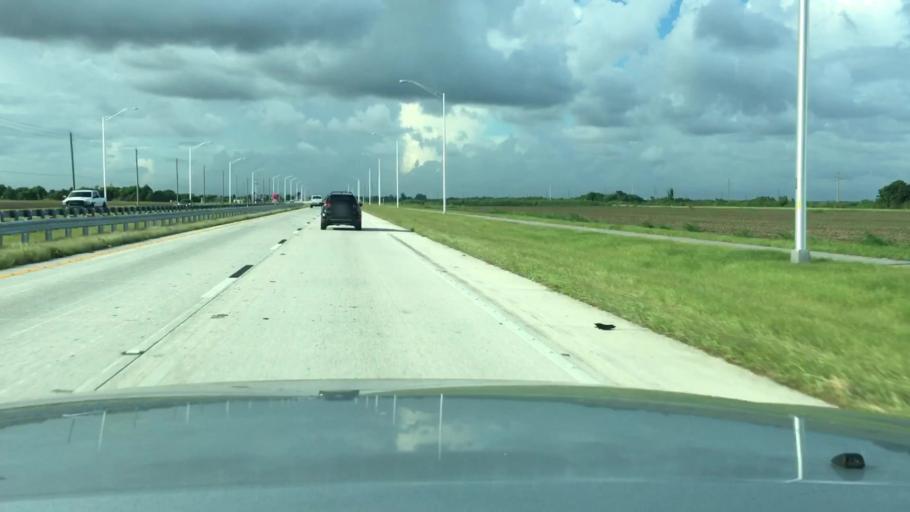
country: US
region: Florida
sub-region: Miami-Dade County
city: The Hammocks
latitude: 25.6555
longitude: -80.4802
